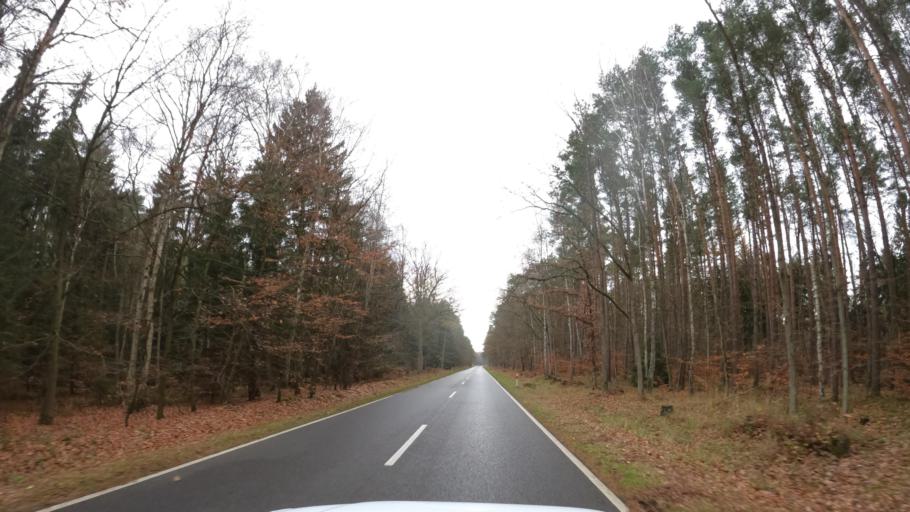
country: PL
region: West Pomeranian Voivodeship
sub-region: Powiat policki
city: Nowe Warpno
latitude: 53.6994
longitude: 14.3375
